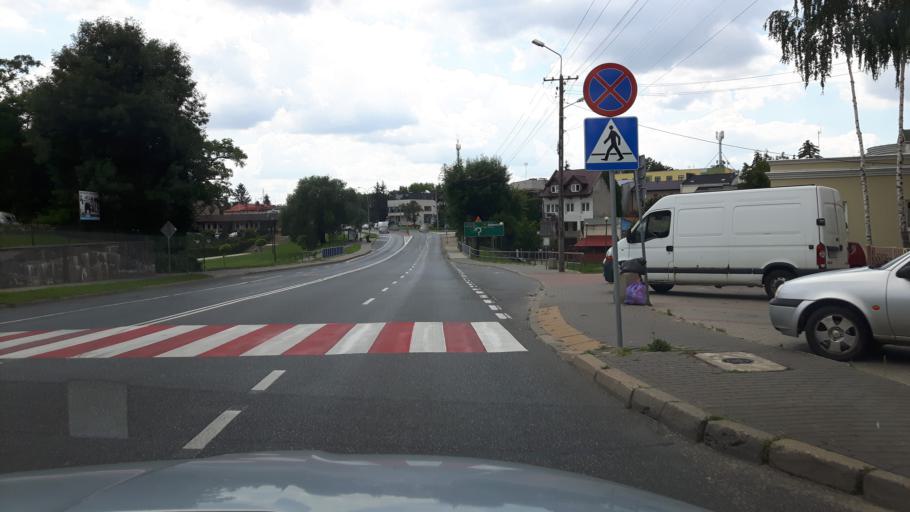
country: PL
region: Masovian Voivodeship
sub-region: Powiat wyszkowski
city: Wyszkow
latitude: 52.5947
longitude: 21.4598
